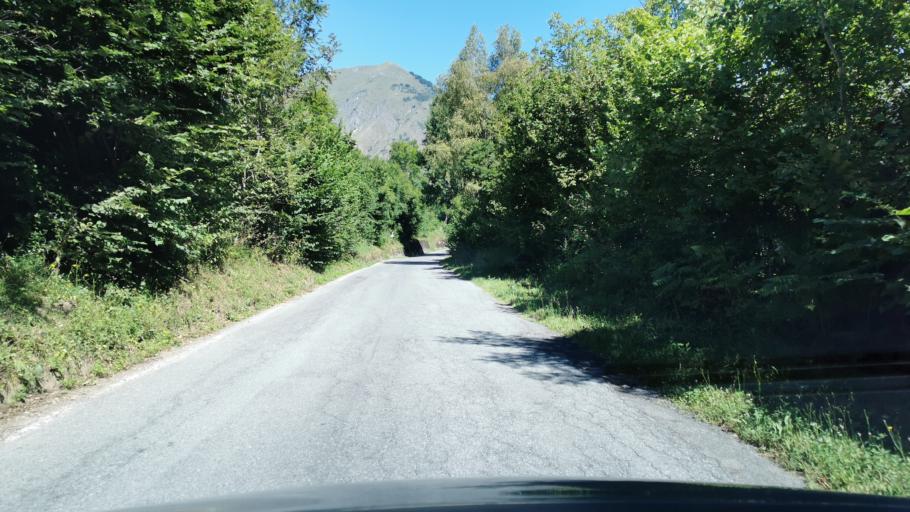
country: IT
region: Piedmont
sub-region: Provincia di Cuneo
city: Entracque
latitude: 44.2433
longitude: 7.3889
